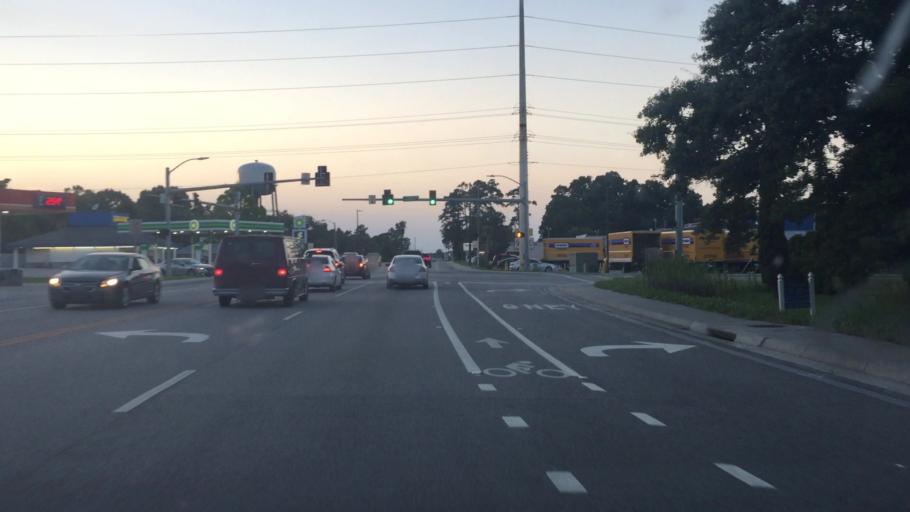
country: US
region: South Carolina
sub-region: Horry County
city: Myrtle Beach
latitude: 33.6906
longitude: -78.8960
